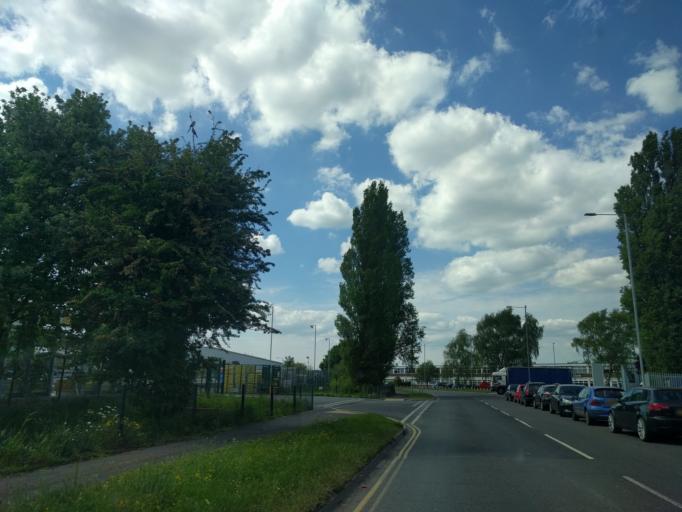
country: GB
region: England
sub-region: Borough of Swindon
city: Swindon
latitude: 51.5750
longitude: -1.7673
